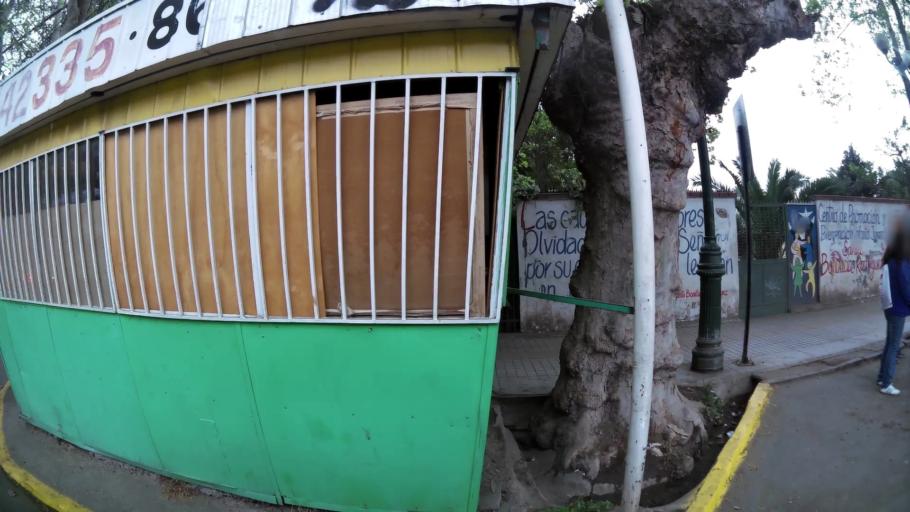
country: CL
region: Santiago Metropolitan
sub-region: Provincia de Chacabuco
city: Chicureo Abajo
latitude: -33.2046
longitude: -70.6765
